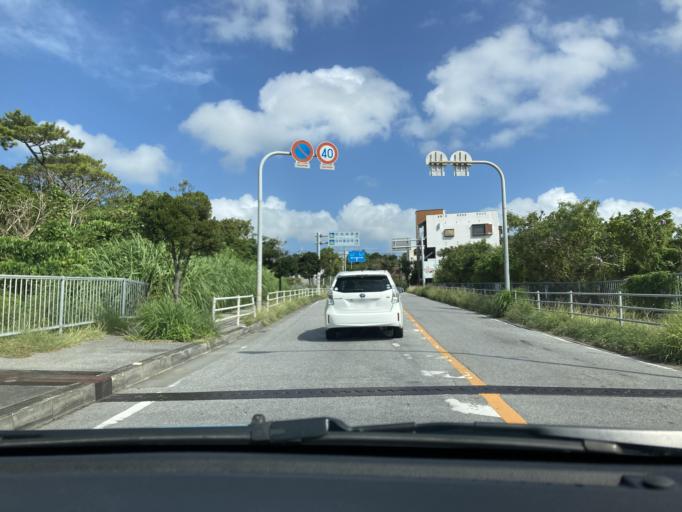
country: JP
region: Okinawa
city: Chatan
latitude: 26.2947
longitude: 127.7845
